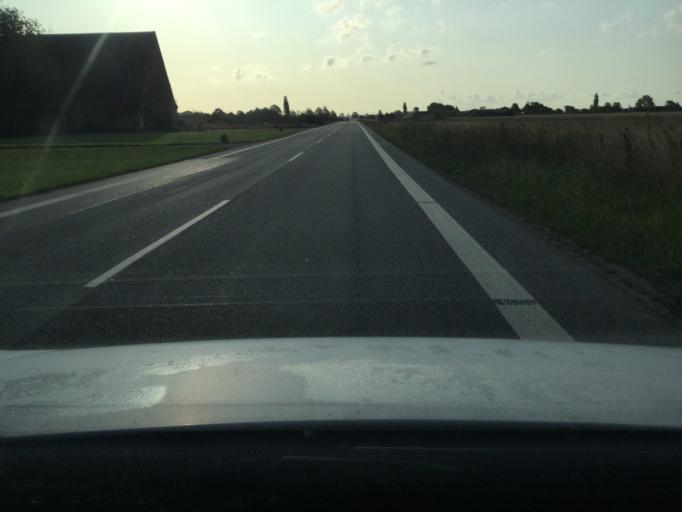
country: DK
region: Zealand
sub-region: Lolland Kommune
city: Rodby
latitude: 54.7554
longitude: 11.3544
